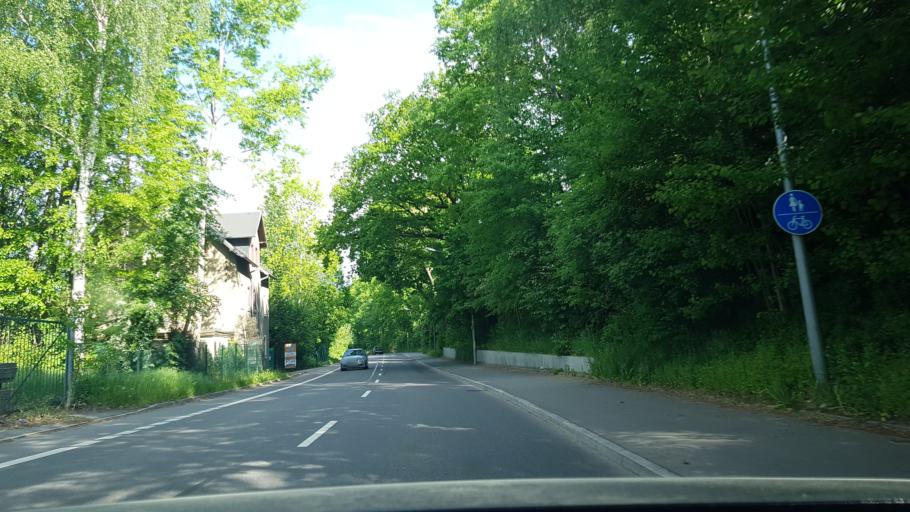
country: DE
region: Saxony
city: Wittgensdorf
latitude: 50.8768
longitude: 12.9053
